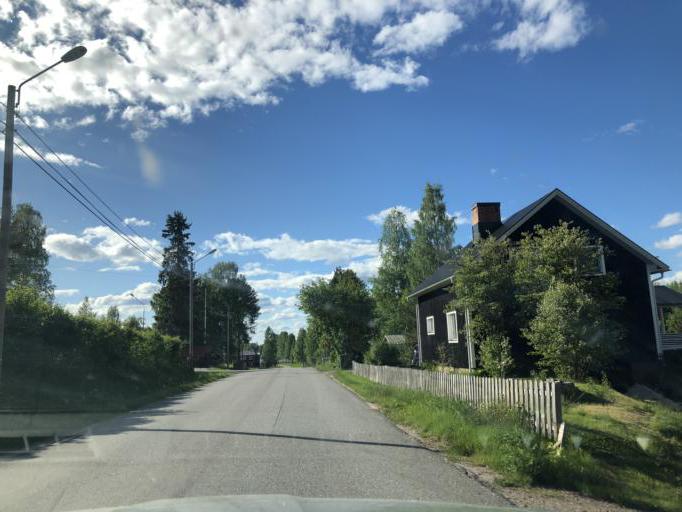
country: SE
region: Norrbotten
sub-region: Overkalix Kommun
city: OEverkalix
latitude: 66.3214
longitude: 22.8606
